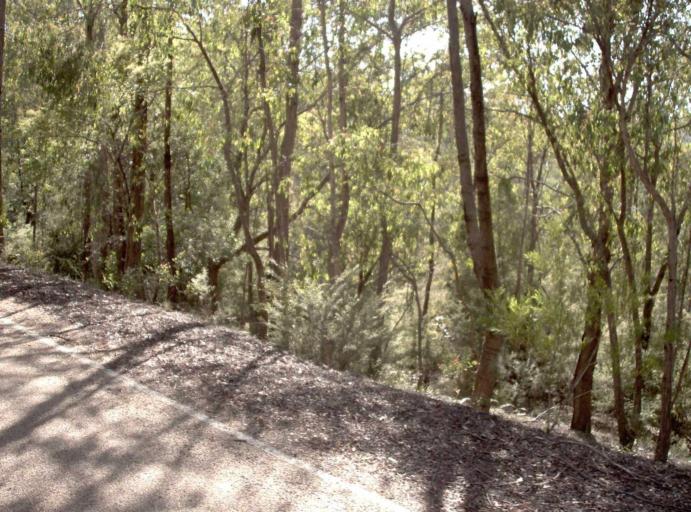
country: AU
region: Victoria
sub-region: East Gippsland
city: Lakes Entrance
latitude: -37.4995
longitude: 148.5512
